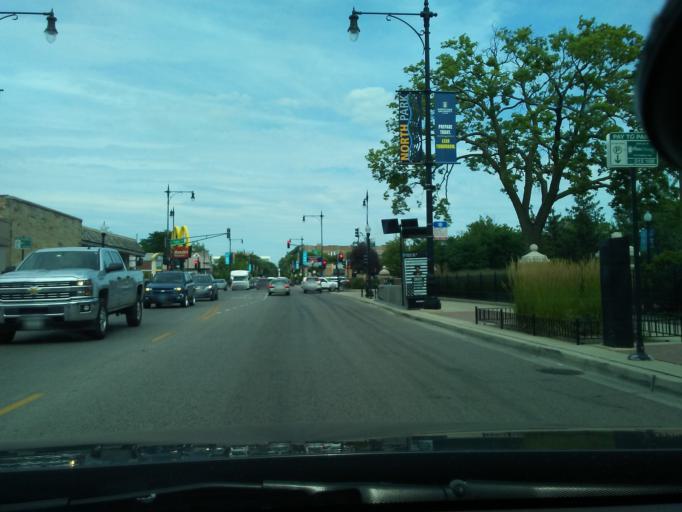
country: US
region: Illinois
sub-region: Cook County
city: Lincolnwood
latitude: 41.9757
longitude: -87.7097
